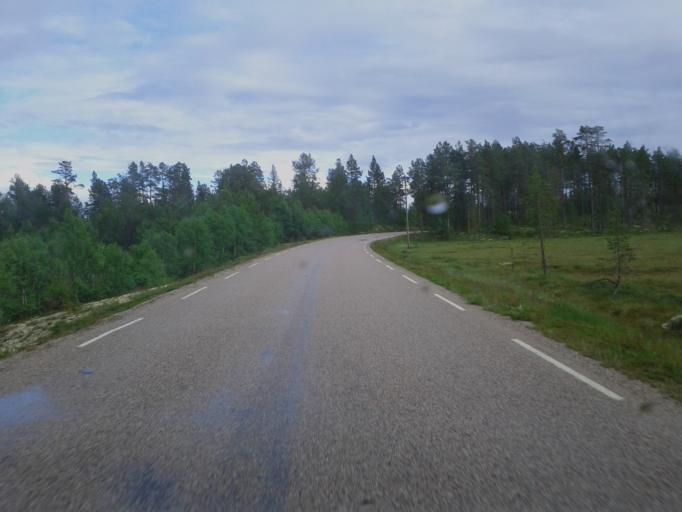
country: NO
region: Hedmark
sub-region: Engerdal
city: Engerdal
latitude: 62.0752
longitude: 11.6728
